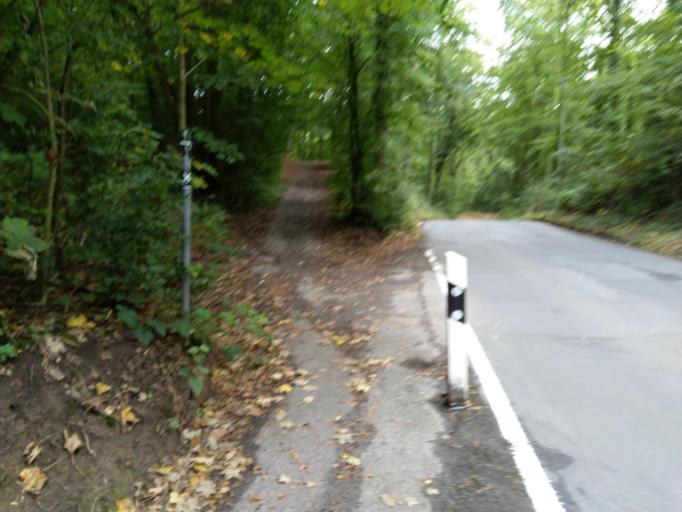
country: DE
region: North Rhine-Westphalia
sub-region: Regierungsbezirk Detmold
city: Bad Salzuflen
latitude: 52.1013
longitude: 8.7676
